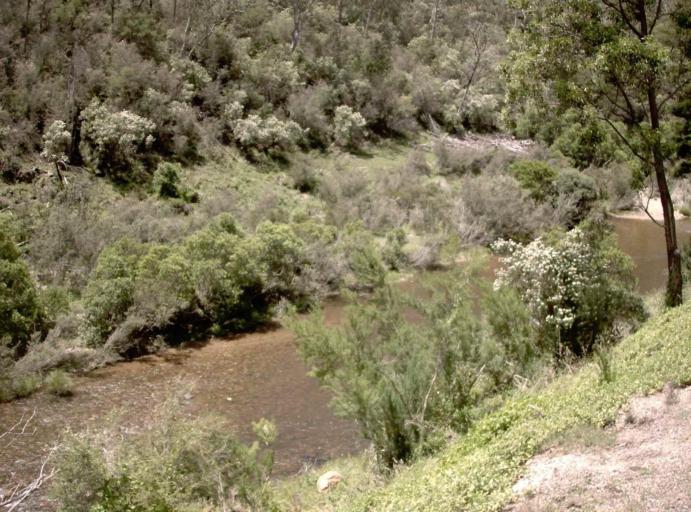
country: AU
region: Victoria
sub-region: East Gippsland
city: Lakes Entrance
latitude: -37.5364
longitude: 147.8635
